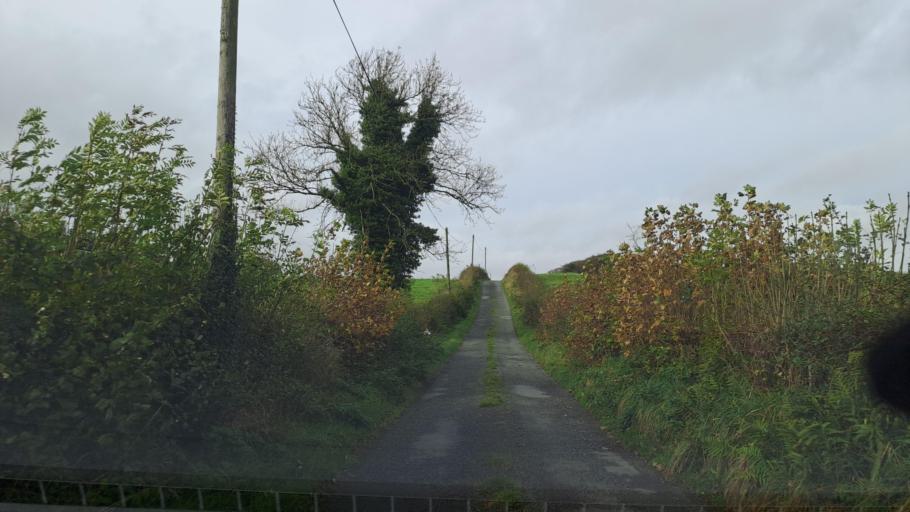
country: IE
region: Ulster
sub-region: County Monaghan
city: Carrickmacross
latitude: 54.0151
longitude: -6.8101
